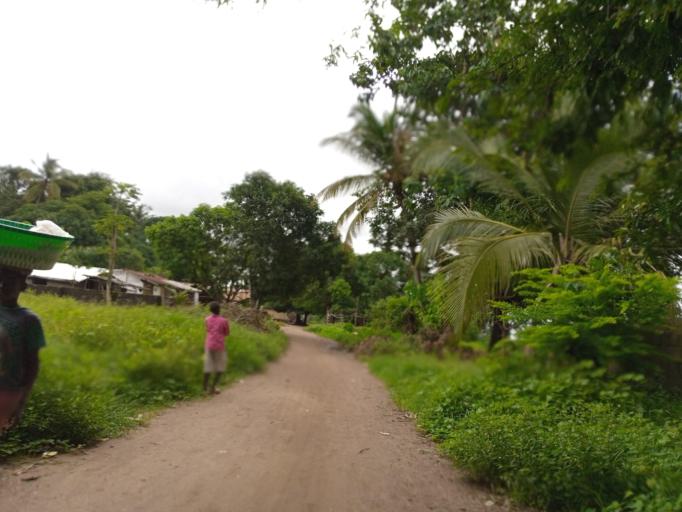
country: SL
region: Northern Province
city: Masoyila
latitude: 8.5868
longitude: -13.1964
